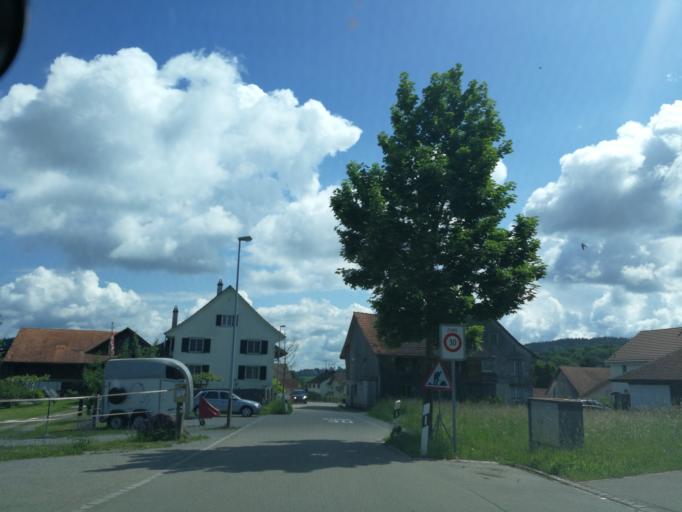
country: CH
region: Zurich
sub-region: Bezirk Meilen
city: Zumikon
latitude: 47.3170
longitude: 8.6272
